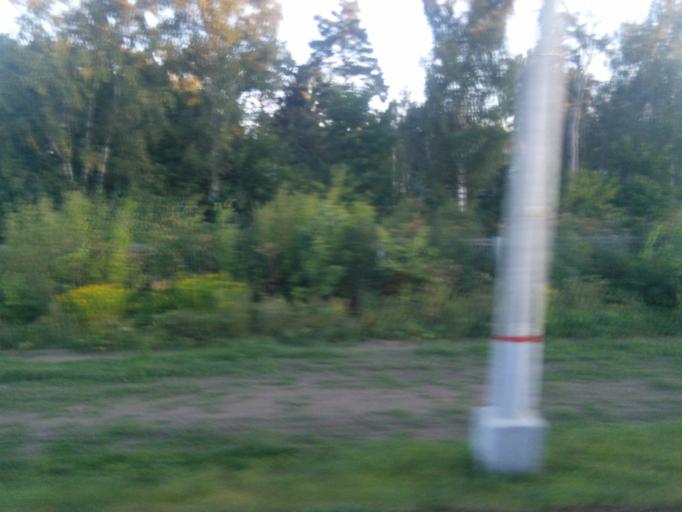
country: RU
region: Moskovskaya
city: Zarya
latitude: 55.7540
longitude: 38.1131
